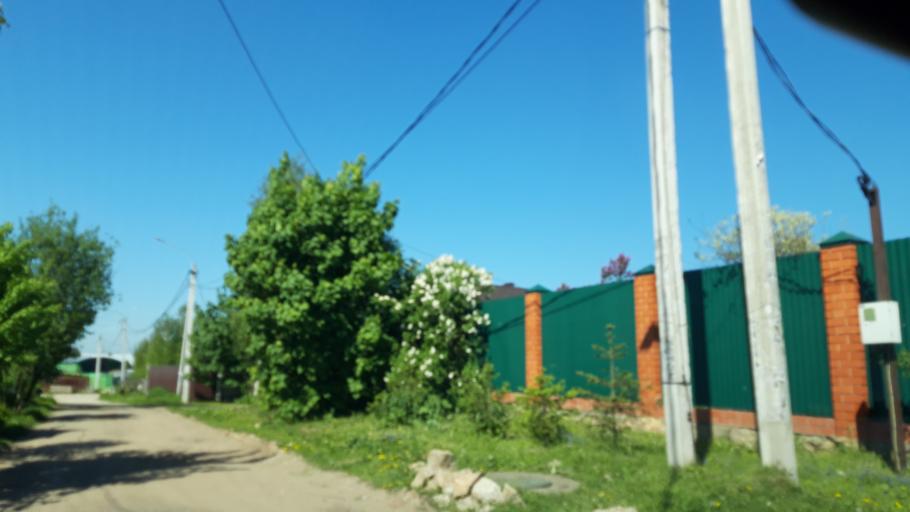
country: RU
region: Moskovskaya
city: Radumlya
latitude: 56.0675
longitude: 37.1221
